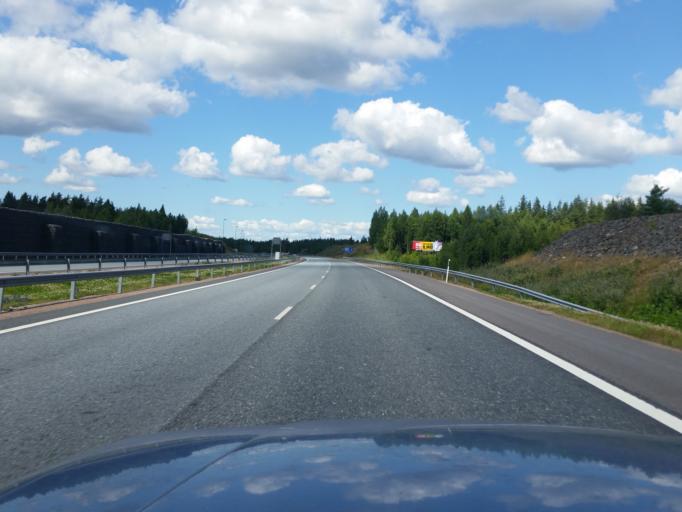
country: FI
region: Uusimaa
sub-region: Helsinki
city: Sammatti
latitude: 60.3663
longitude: 23.8737
